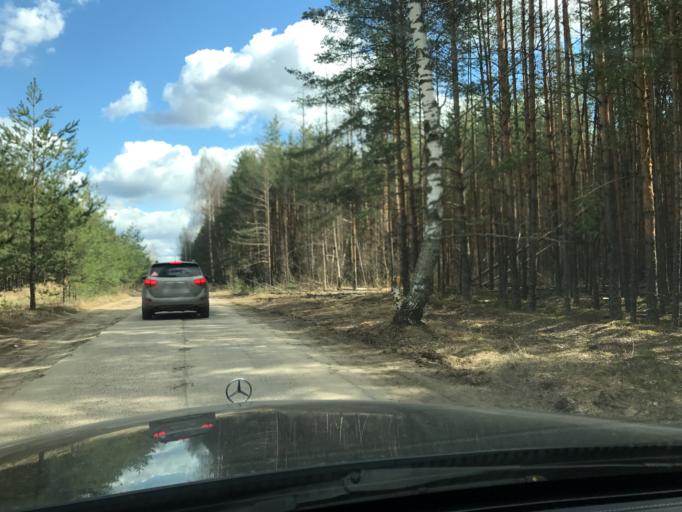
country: RU
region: Vladimir
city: Pokrov
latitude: 55.8626
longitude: 39.2136
